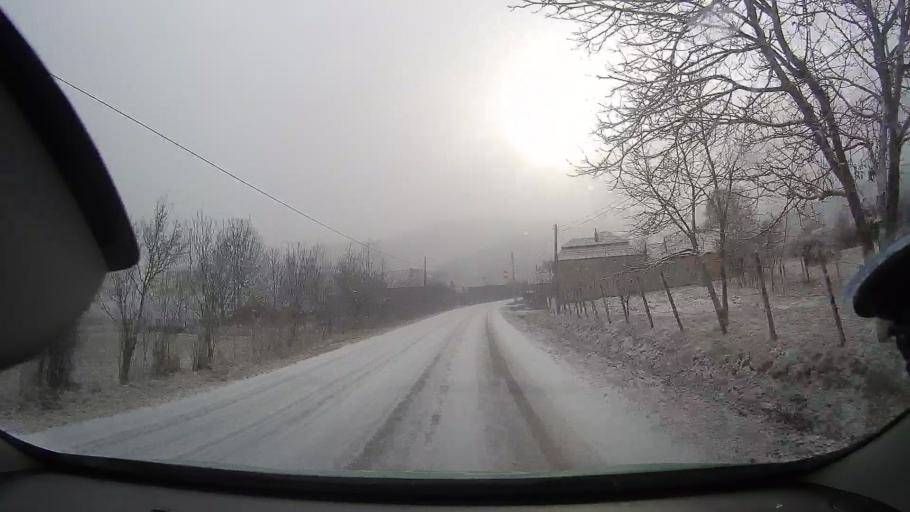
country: RO
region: Alba
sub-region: Comuna Rimetea
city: Rimetea
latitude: 46.3923
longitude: 23.5615
